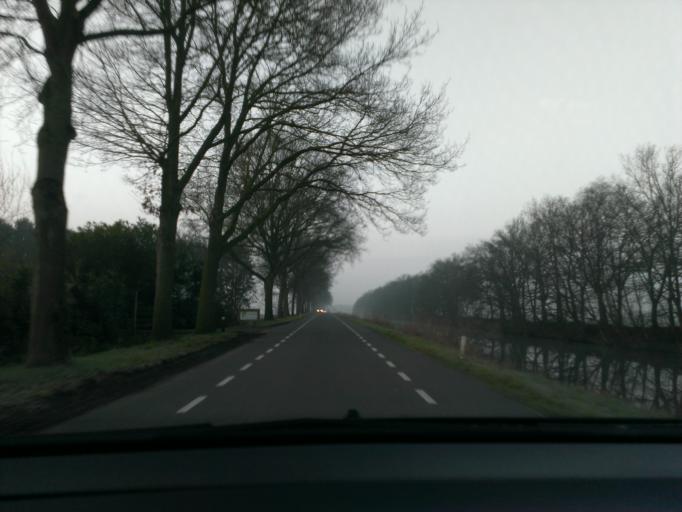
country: NL
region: Gelderland
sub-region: Gemeente Epe
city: Epe
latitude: 52.3267
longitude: 6.0137
